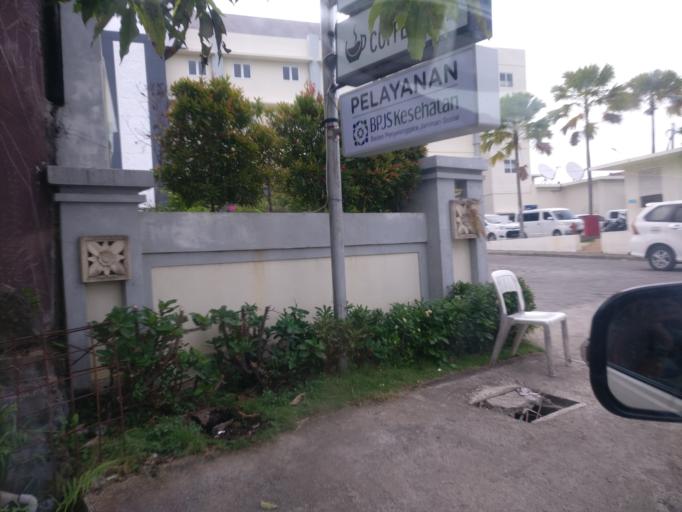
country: ID
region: Bali
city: Banjar Pasekan
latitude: -8.6051
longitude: 115.3139
